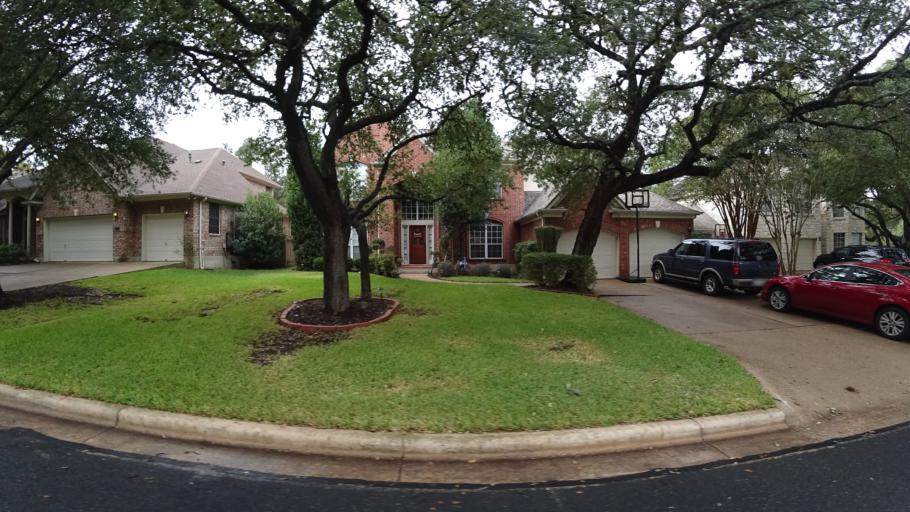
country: US
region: Texas
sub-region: Travis County
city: Shady Hollow
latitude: 30.1948
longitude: -97.8756
